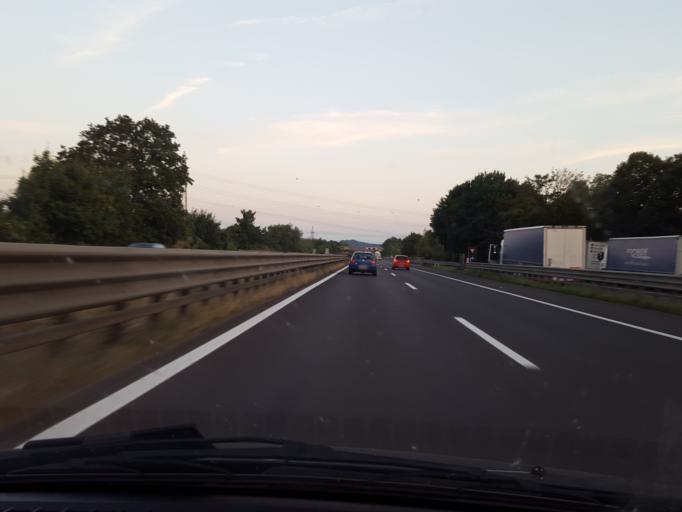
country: AT
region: Upper Austria
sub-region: Politischer Bezirk Linz-Land
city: Ansfelden
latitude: 48.2443
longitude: 14.2974
